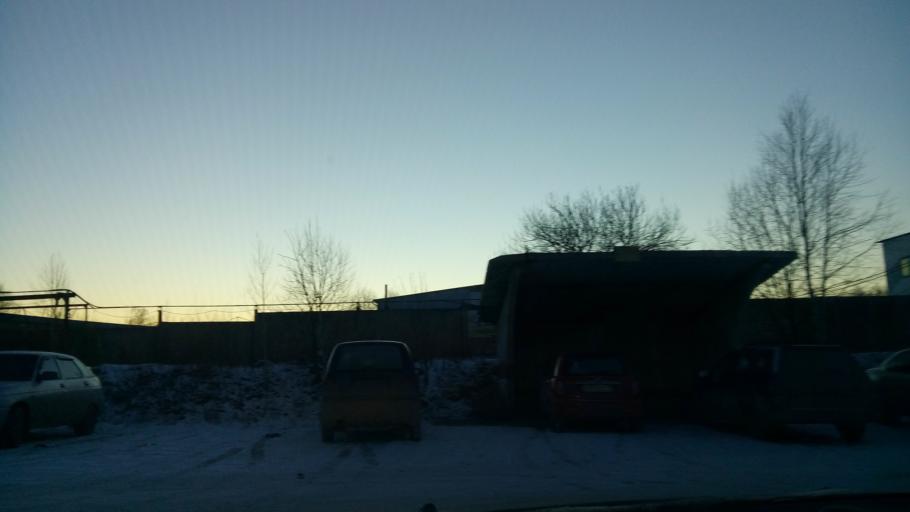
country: RU
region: Sverdlovsk
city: Polevskoy
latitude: 56.4717
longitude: 60.1745
